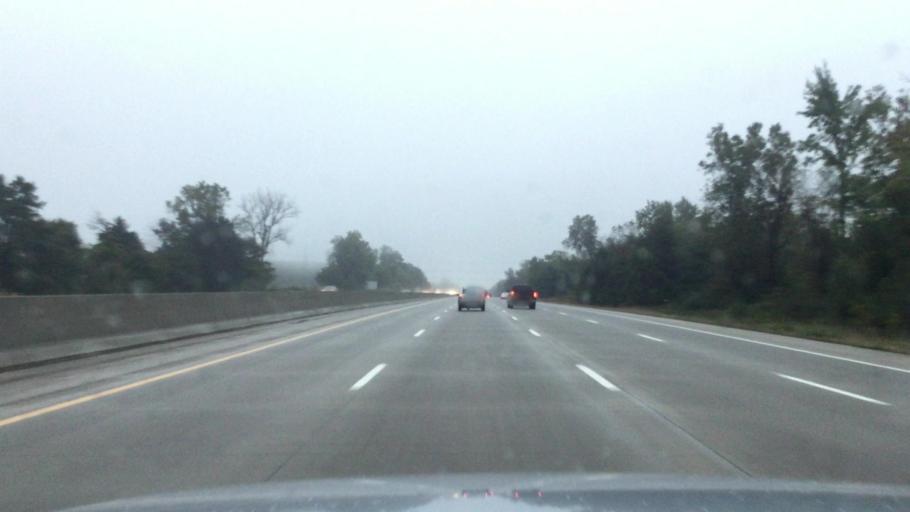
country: US
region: Michigan
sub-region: Genesee County
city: Clio
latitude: 43.1936
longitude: -83.7689
